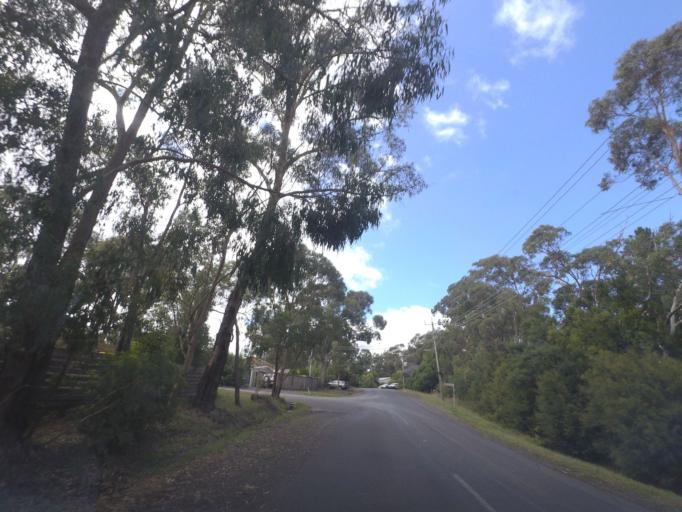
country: AU
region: Victoria
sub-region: Yarra Ranges
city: Launching Place
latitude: -37.7816
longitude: 145.5566
